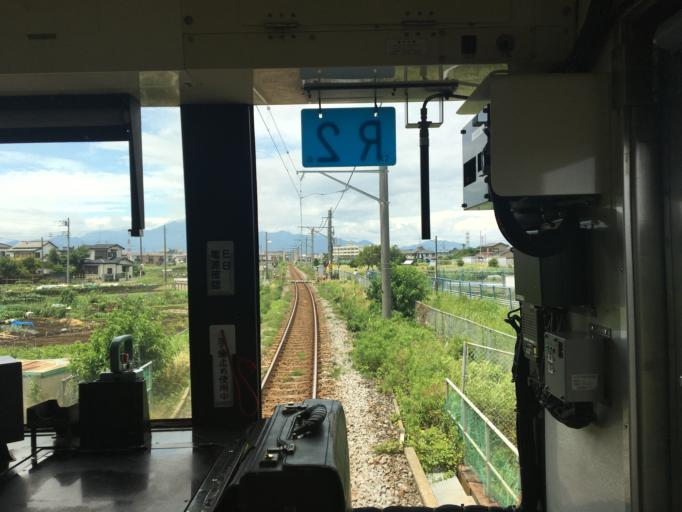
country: JP
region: Kanagawa
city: Chigasaki
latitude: 35.3608
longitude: 139.3973
